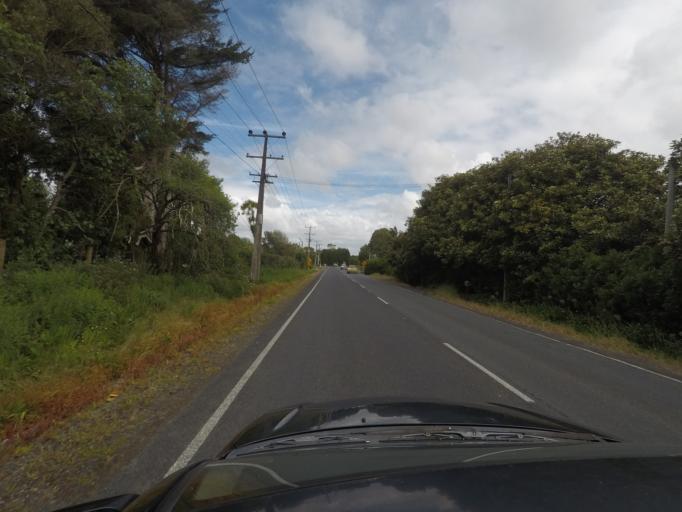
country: NZ
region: Auckland
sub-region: Auckland
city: Muriwai Beach
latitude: -36.7715
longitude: 174.5733
